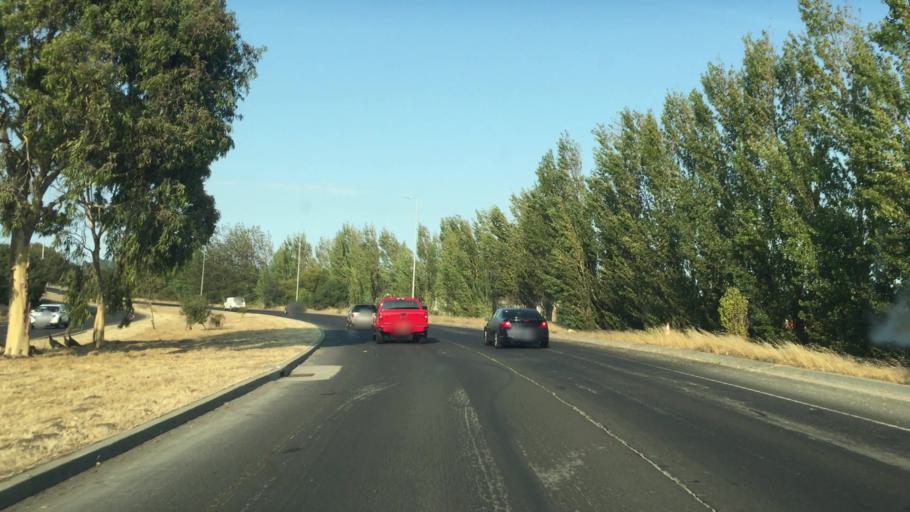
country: US
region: California
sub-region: Contra Costa County
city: North Richmond
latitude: 37.9743
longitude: -122.3634
